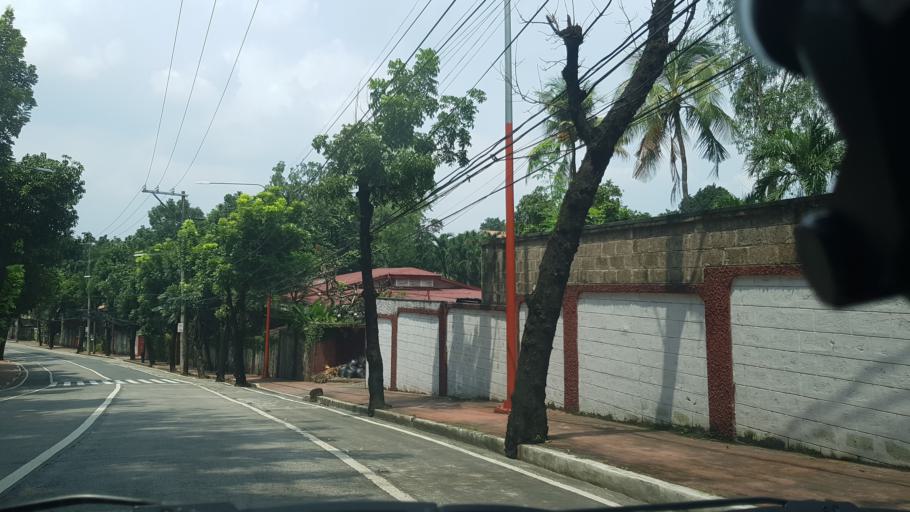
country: PH
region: Calabarzon
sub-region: Province of Rizal
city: Antipolo
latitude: 14.6563
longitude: 121.1218
